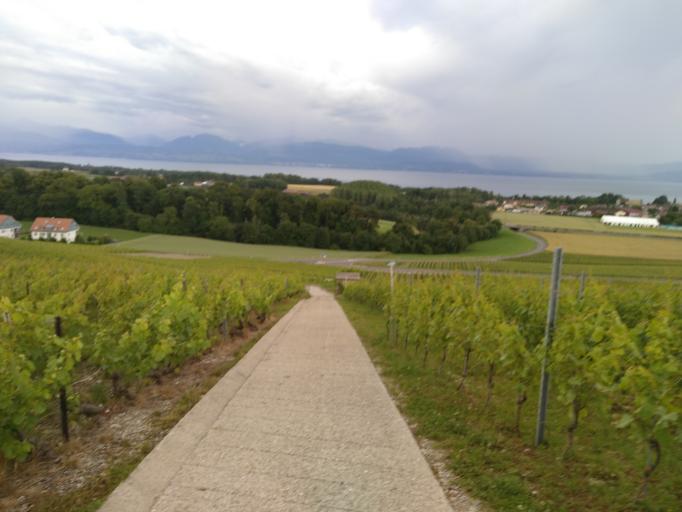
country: CH
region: Vaud
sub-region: Nyon District
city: Perroy
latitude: 46.4792
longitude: 6.3661
